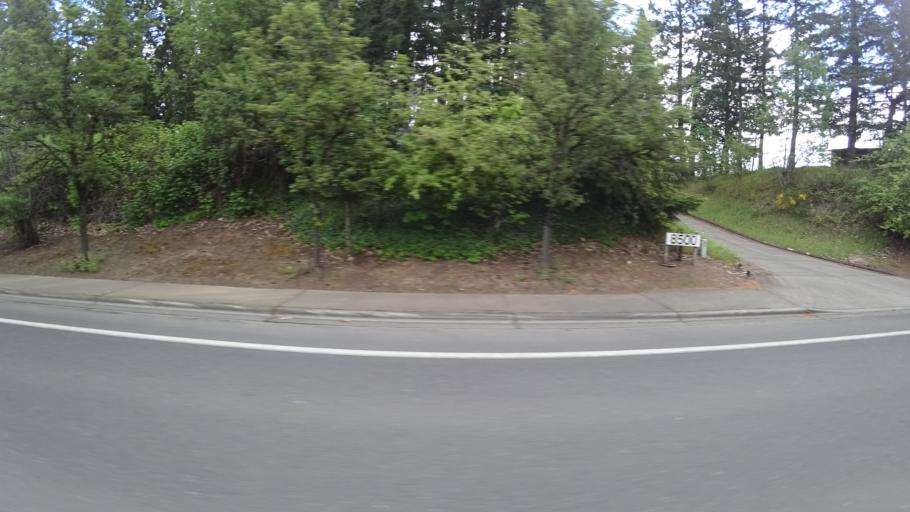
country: US
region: Oregon
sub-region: Washington County
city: Beaverton
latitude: 45.4586
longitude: -122.8262
